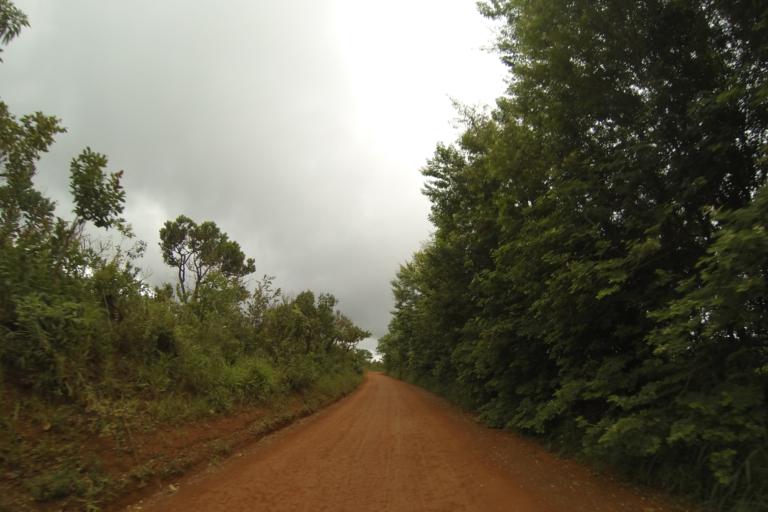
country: BR
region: Minas Gerais
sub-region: Campos Altos
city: Campos Altos
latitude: -19.8211
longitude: -46.3286
